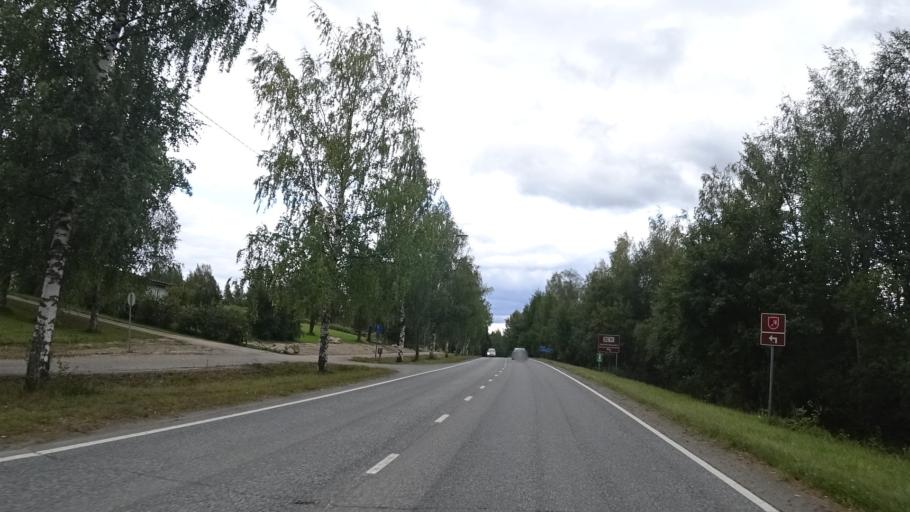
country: FI
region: North Karelia
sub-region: Joensuu
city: Ilomantsi
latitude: 62.6565
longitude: 30.9337
